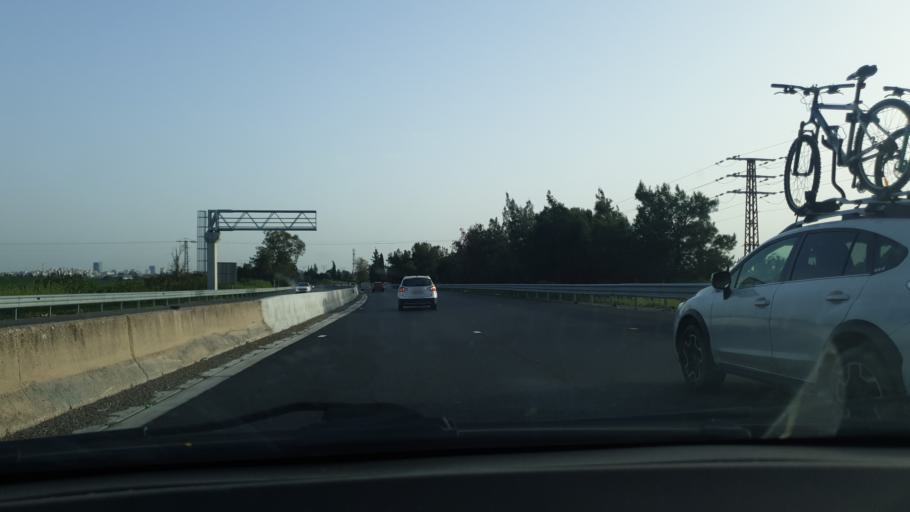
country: IL
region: Central District
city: Tel Mond
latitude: 32.2279
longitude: 34.8831
